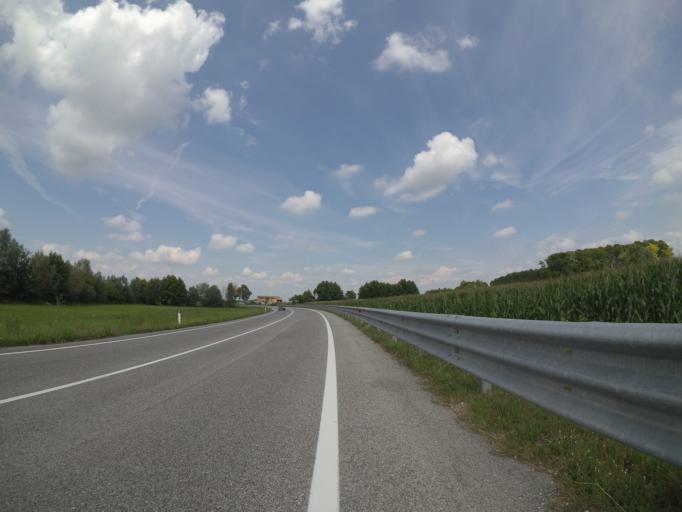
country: IT
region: Friuli Venezia Giulia
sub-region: Provincia di Udine
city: Varmo
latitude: 45.8932
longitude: 13.0107
